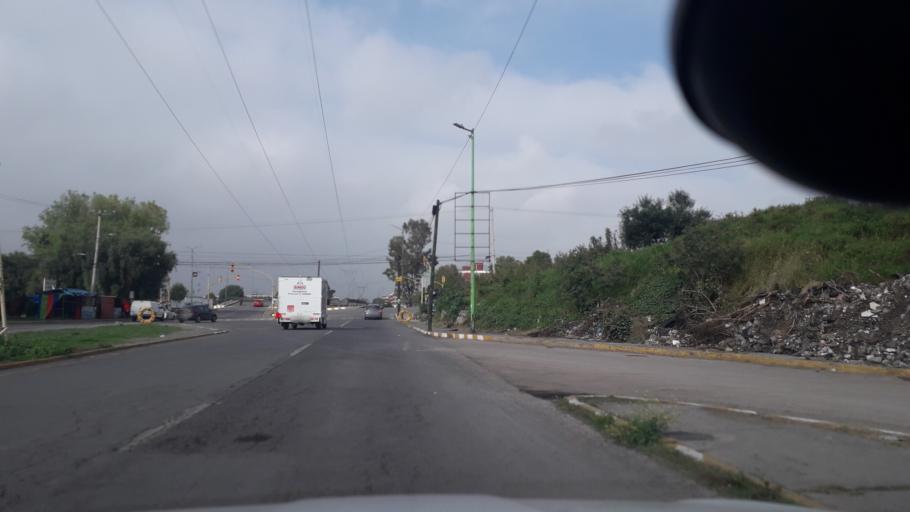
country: MX
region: Mexico
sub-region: Jaltenco
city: Alborada Jaltenco
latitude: 19.6449
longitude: -99.0792
